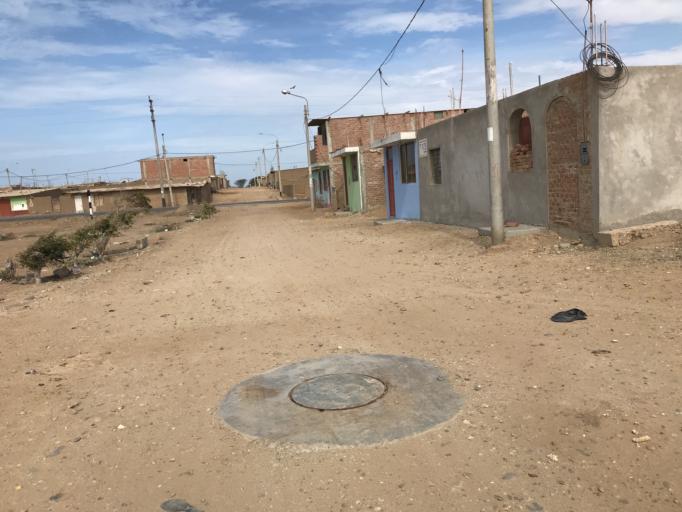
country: PE
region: Lambayeque
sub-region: Provincia de Chiclayo
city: Eten
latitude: -6.8987
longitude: -79.8437
